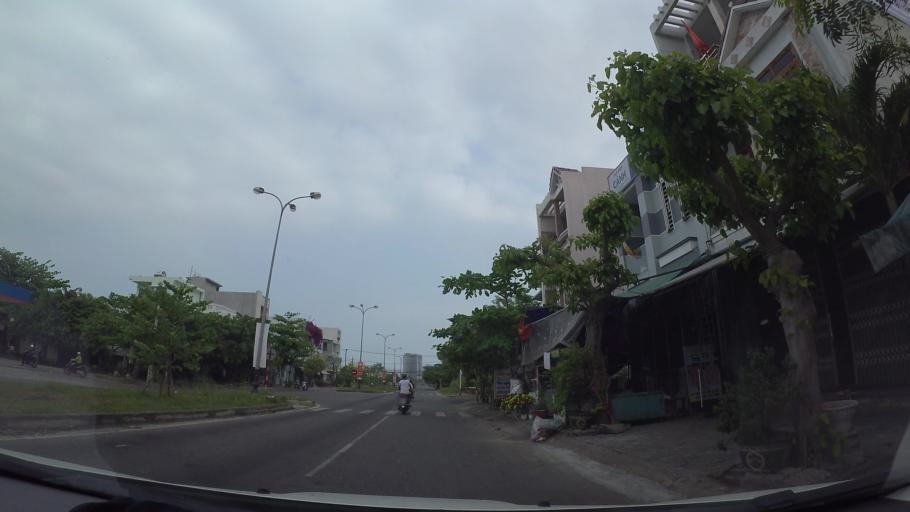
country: VN
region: Da Nang
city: Da Nang
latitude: 16.0874
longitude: 108.2338
